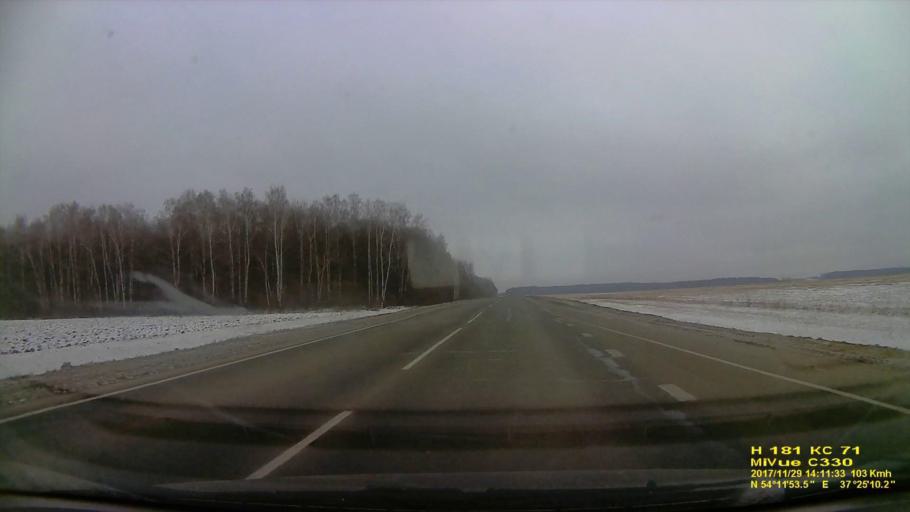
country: RU
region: Tula
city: Barsuki
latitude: 54.1980
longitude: 37.4198
